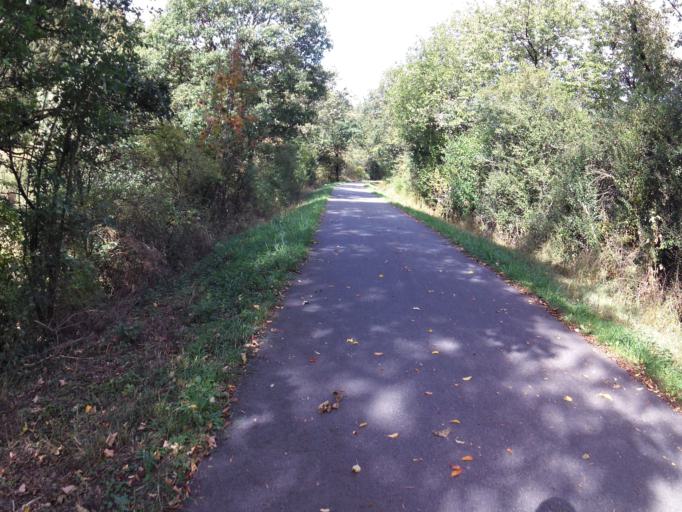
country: DE
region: Rheinland-Pfalz
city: Kickeshausen
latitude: 50.0597
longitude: 6.2477
